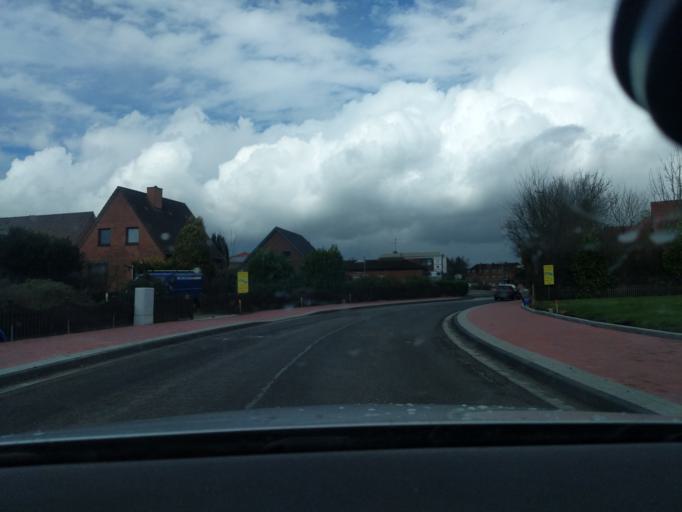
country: DE
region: Lower Saxony
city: Stade
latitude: 53.6130
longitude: 9.4721
